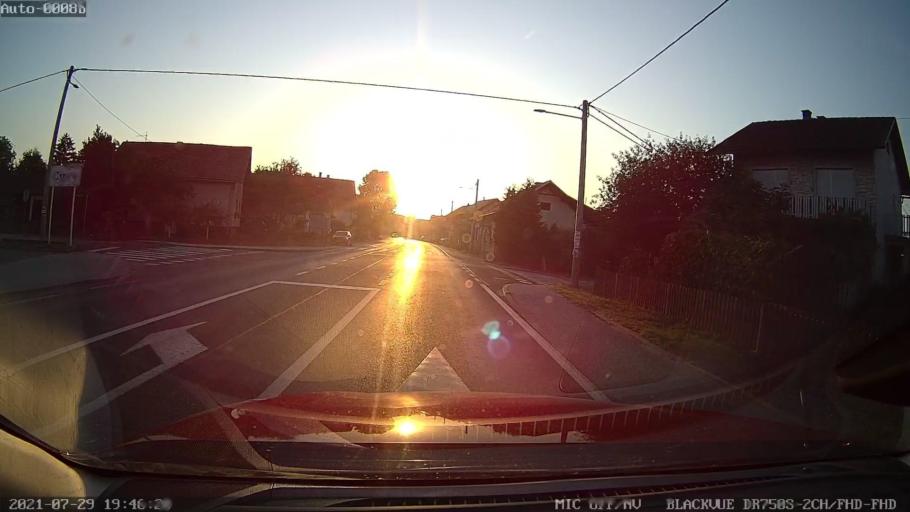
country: HR
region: Varazdinska
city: Ludbreg
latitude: 46.2633
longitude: 16.5756
